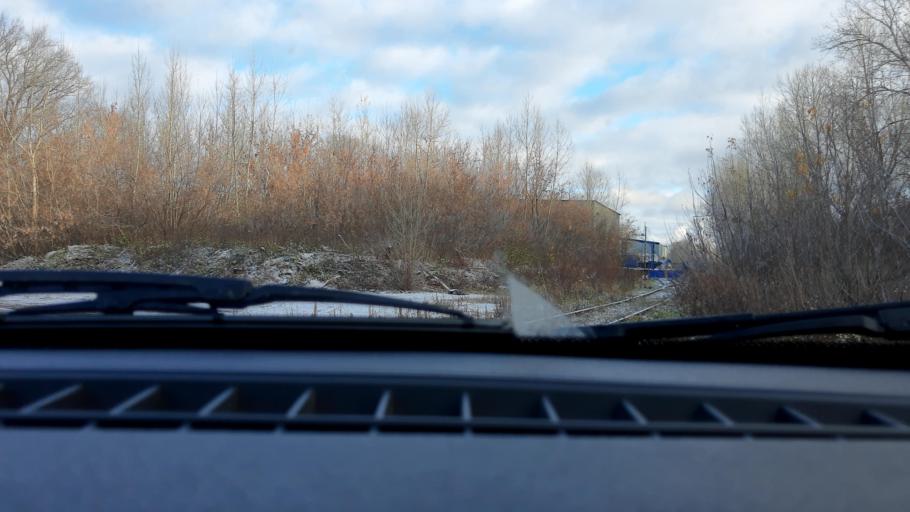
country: RU
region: Bashkortostan
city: Ufa
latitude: 54.7586
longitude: 55.9733
